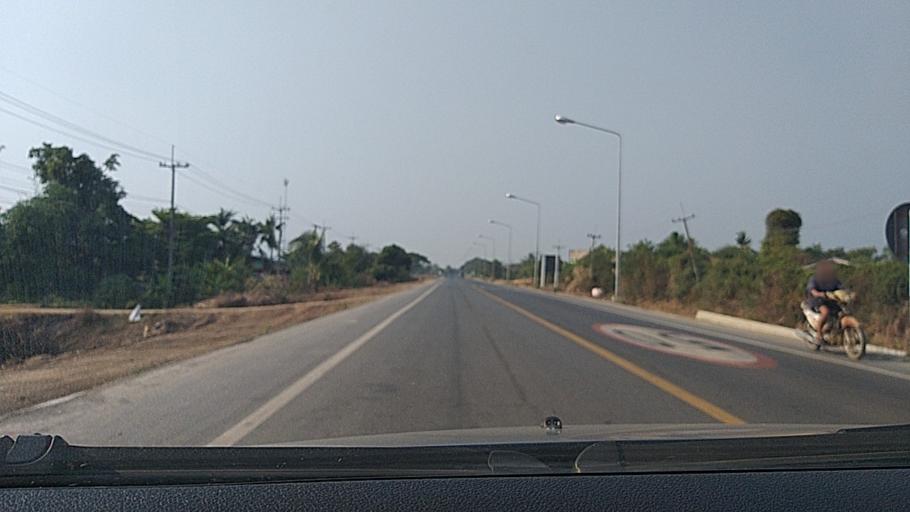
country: TH
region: Sing Buri
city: Phrom Buri
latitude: 14.7714
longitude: 100.4380
